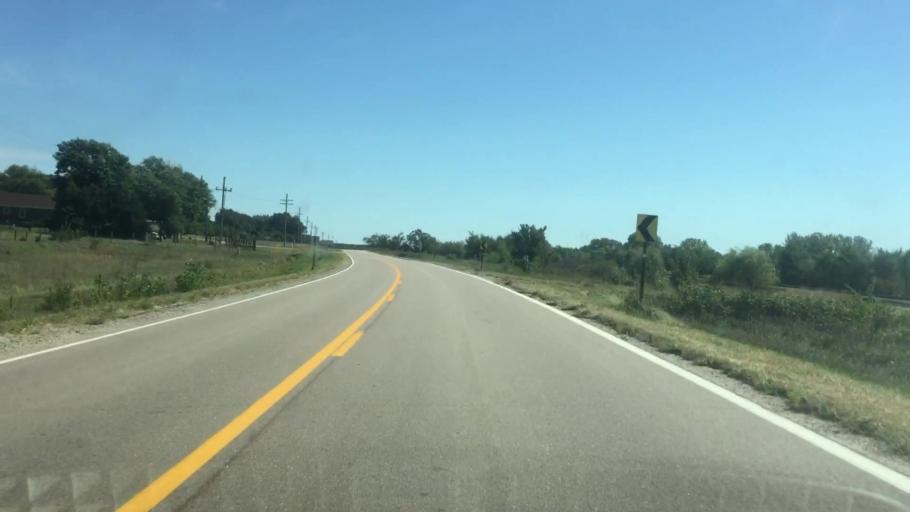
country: US
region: Nebraska
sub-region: Jefferson County
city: Fairbury
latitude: 40.0814
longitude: -97.1047
